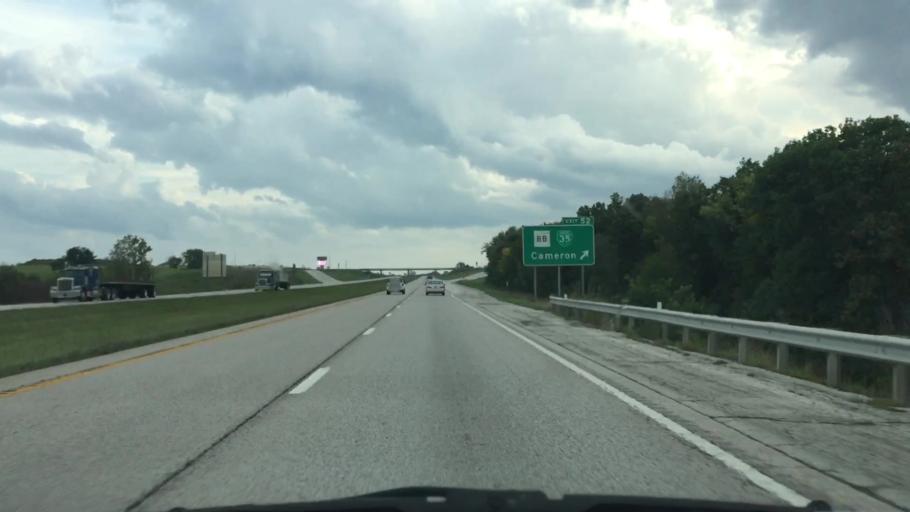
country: US
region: Missouri
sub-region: Clinton County
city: Cameron
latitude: 39.7377
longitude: -94.2205
